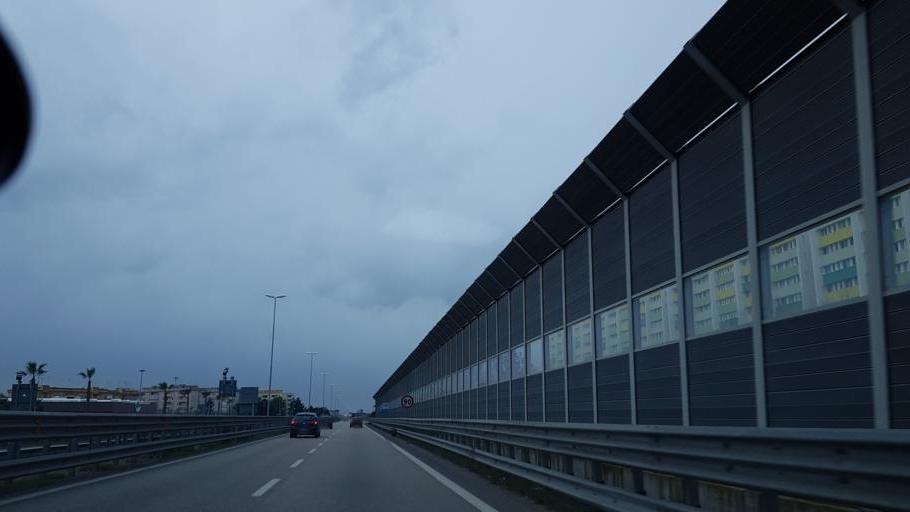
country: IT
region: Apulia
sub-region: Provincia di Brindisi
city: Brindisi
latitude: 40.6244
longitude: 17.9166
